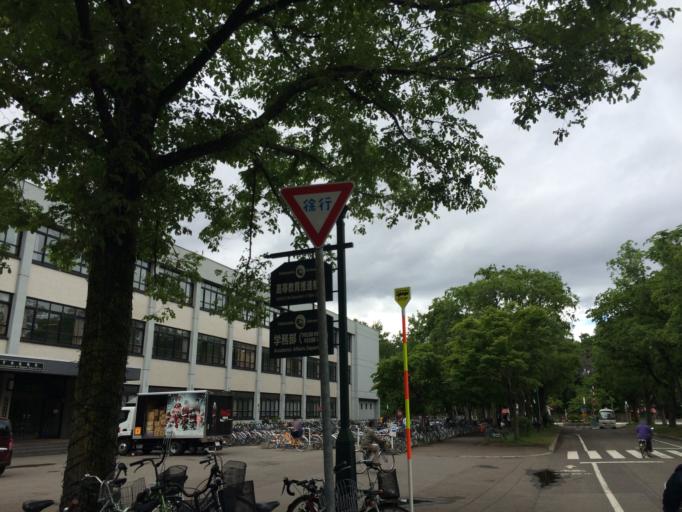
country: JP
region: Hokkaido
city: Sapporo
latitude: 43.0795
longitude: 141.3408
